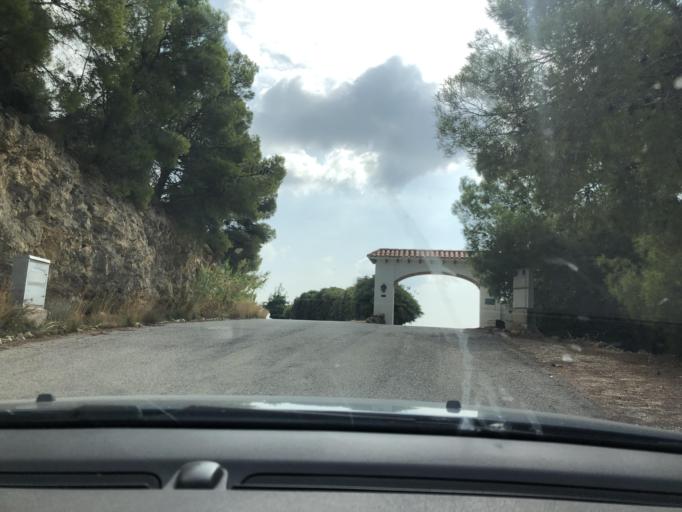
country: ES
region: Valencia
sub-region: Provincia de Alicante
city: Callosa d'En Sarria
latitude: 38.6331
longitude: -0.1119
